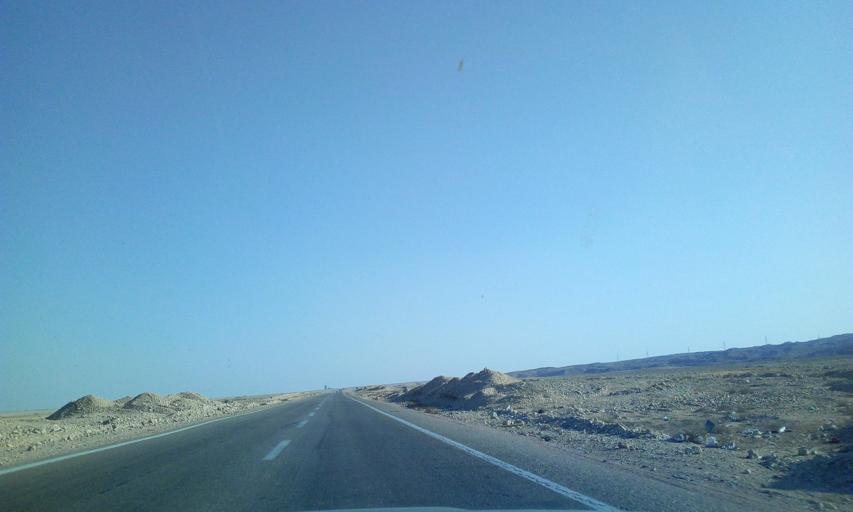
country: EG
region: As Suways
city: Ain Sukhna
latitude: 28.9558
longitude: 32.6220
